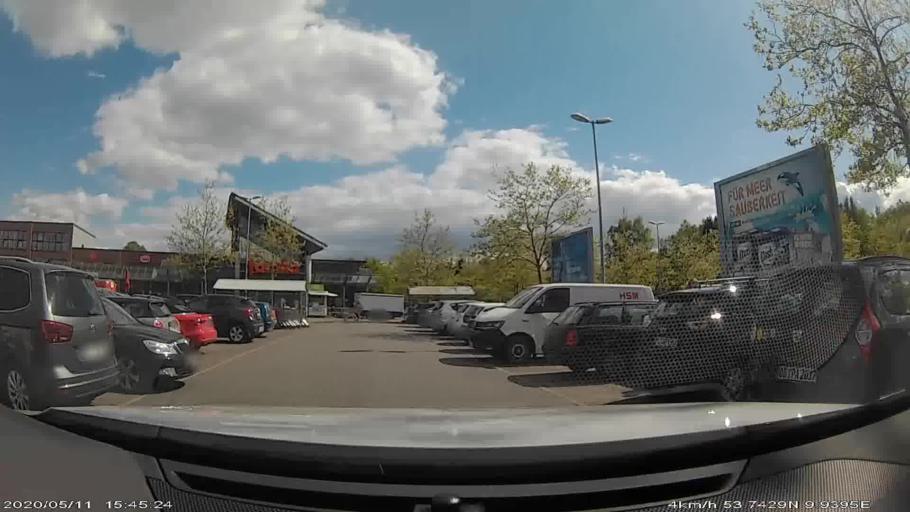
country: DE
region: Schleswig-Holstein
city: Ellerau
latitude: 53.7389
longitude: 9.9626
